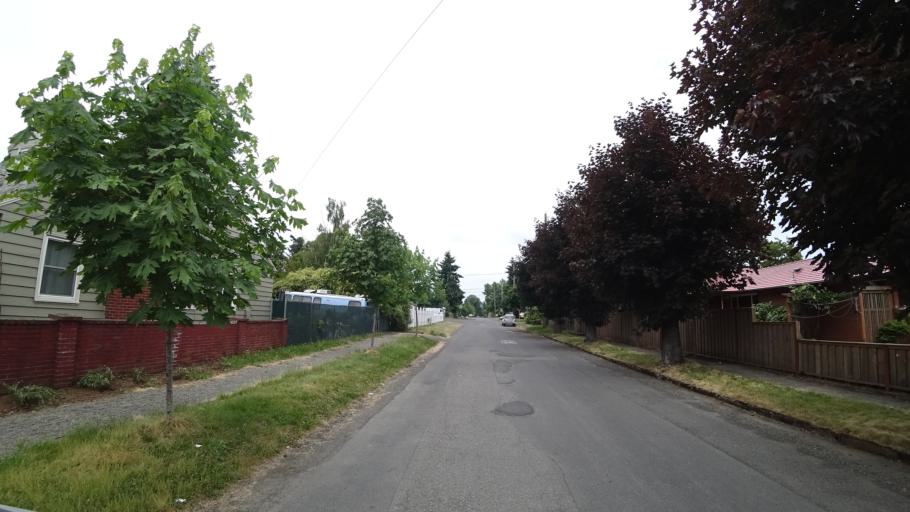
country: US
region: Oregon
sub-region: Multnomah County
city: Lents
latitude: 45.5094
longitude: -122.5741
